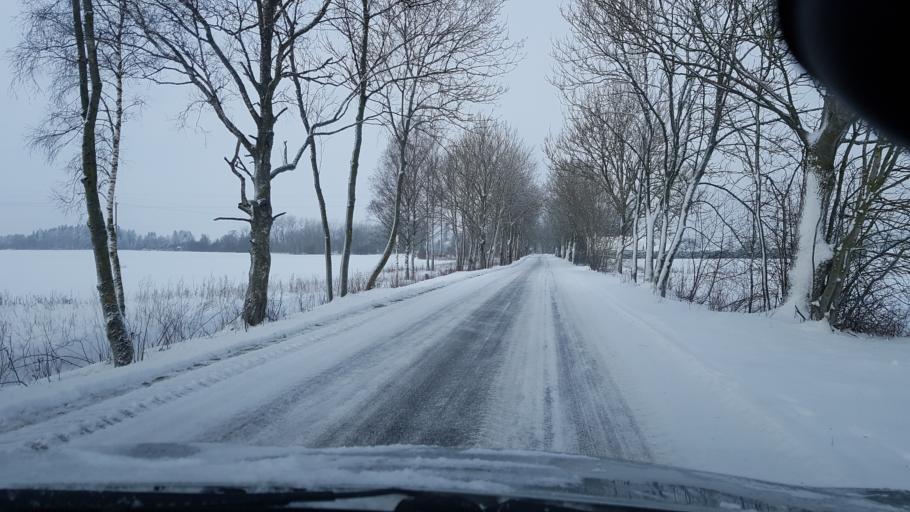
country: EE
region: Harju
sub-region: Keila linn
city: Keila
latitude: 59.3286
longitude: 24.4471
